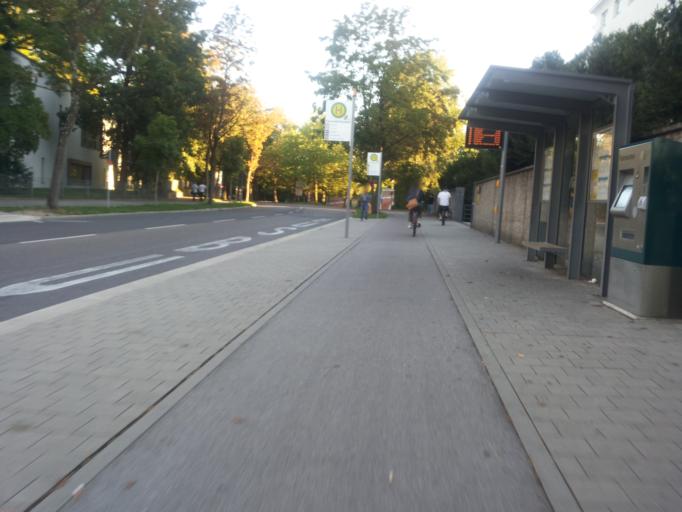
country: DE
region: Bavaria
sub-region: Upper Bavaria
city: Ingolstadt
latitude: 48.7656
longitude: 11.4166
